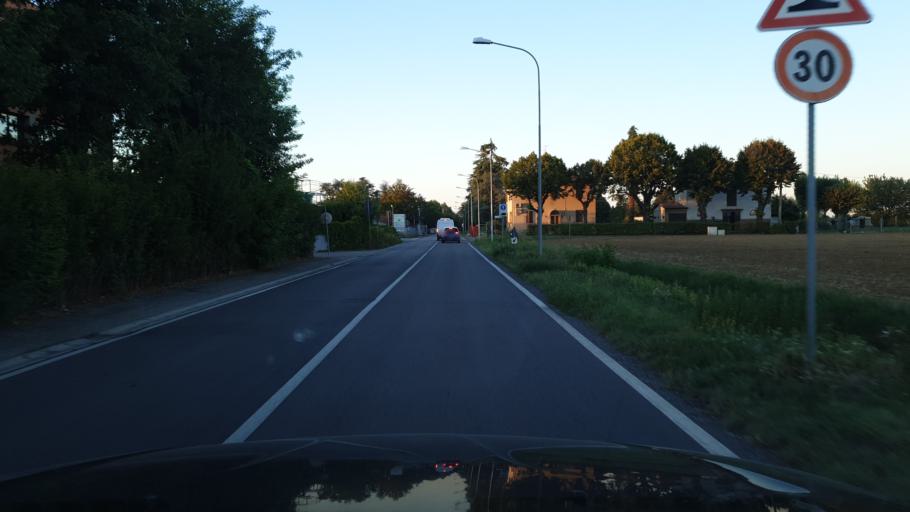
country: IT
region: Emilia-Romagna
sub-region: Provincia di Bologna
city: Quarto Inferiore
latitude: 44.5451
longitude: 11.3966
